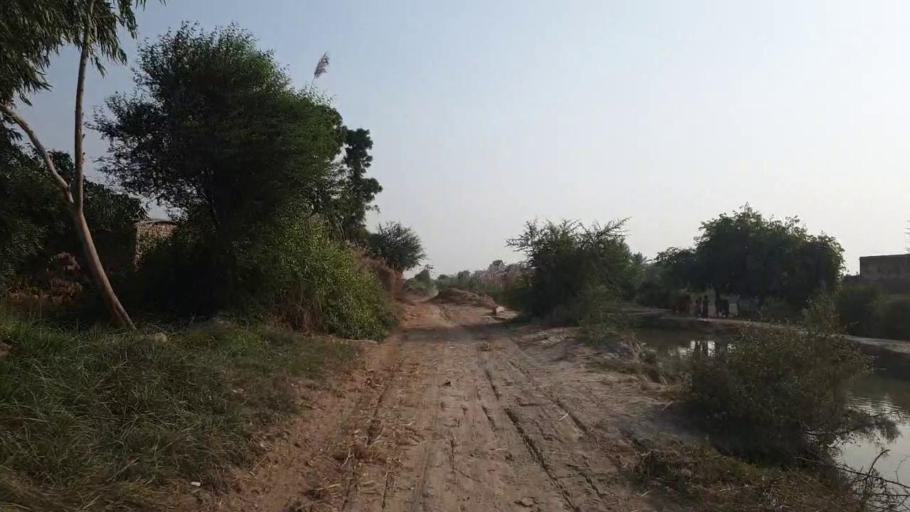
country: PK
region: Sindh
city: Tando Muhammad Khan
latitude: 25.0875
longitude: 68.3584
